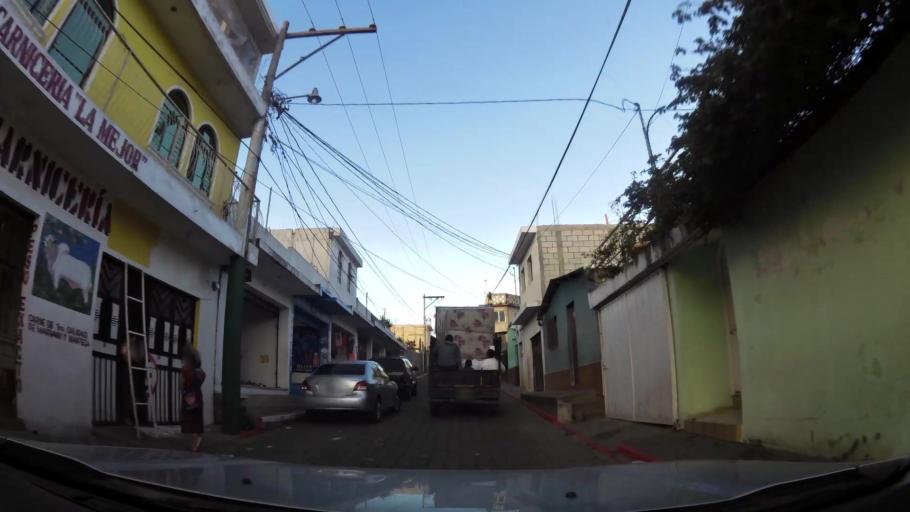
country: GT
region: Sacatepequez
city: San Lucas Sacatepequez
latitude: 14.6105
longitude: -90.6549
